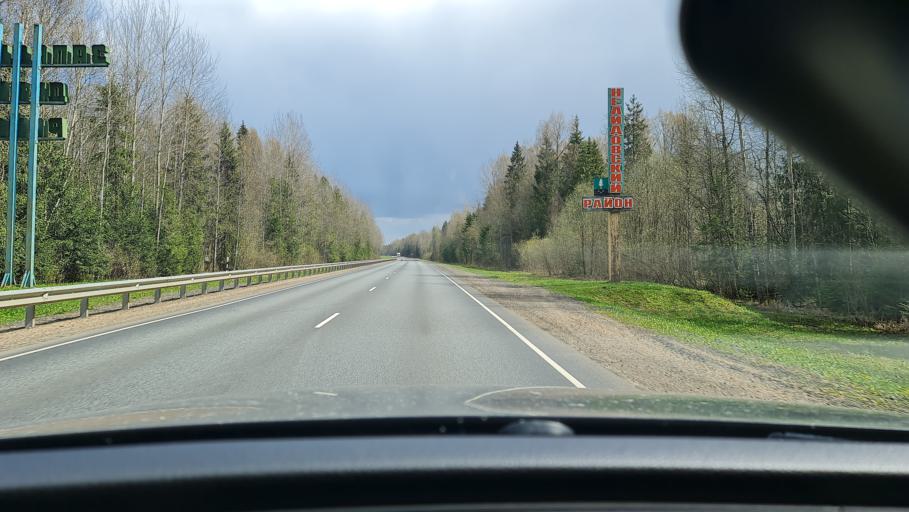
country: RU
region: Tverskaya
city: Zapadnaya Dvina
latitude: 56.3025
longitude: 32.3686
